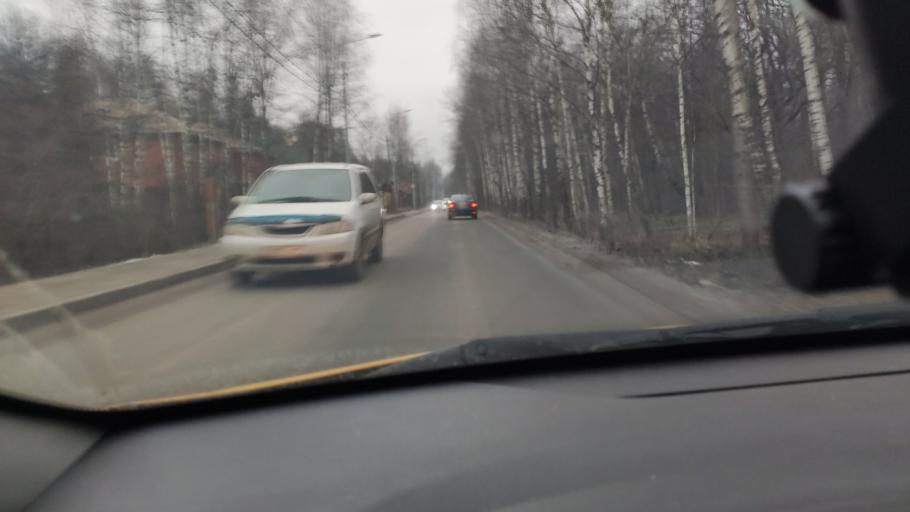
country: RU
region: Moscow
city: Annino
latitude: 55.5479
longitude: 37.6194
